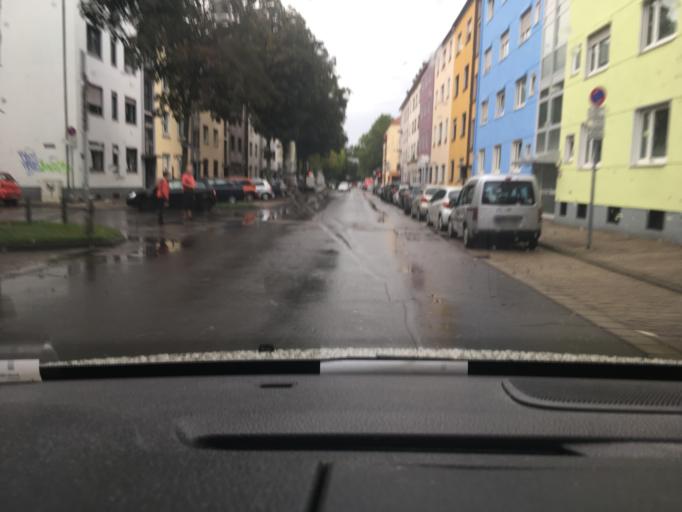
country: DE
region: Saarland
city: Saarbrucken
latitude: 49.2328
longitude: 6.9756
